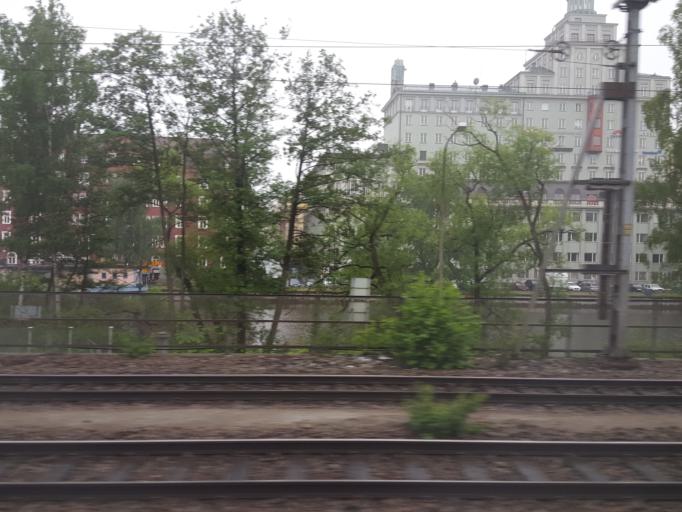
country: SE
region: Stockholm
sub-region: Stockholms Kommun
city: Stockholm
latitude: 59.3375
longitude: 18.0364
